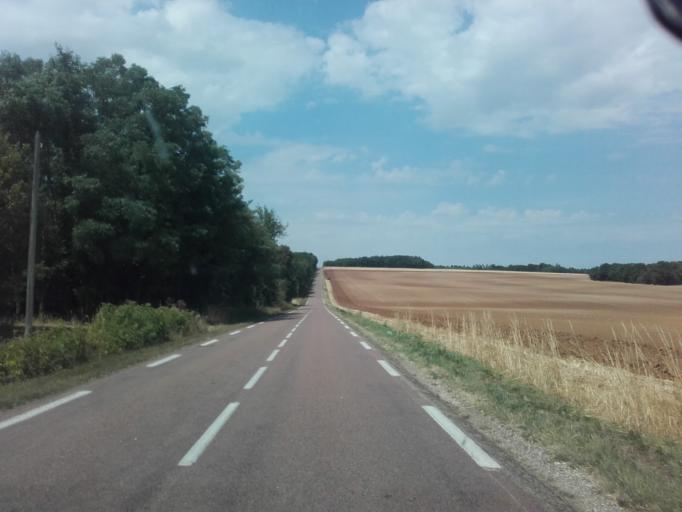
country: FR
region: Bourgogne
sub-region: Departement de l'Yonne
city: Joux-la-Ville
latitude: 47.6961
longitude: 3.8624
